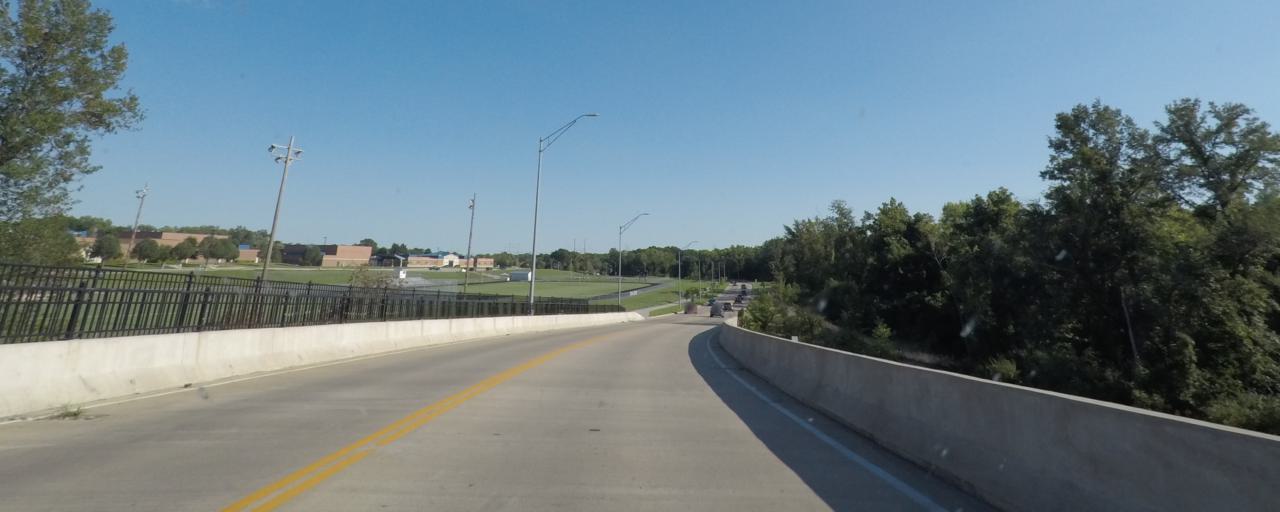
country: US
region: Missouri
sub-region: Clay County
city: Pleasant Valley
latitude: 39.2274
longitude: -94.4663
